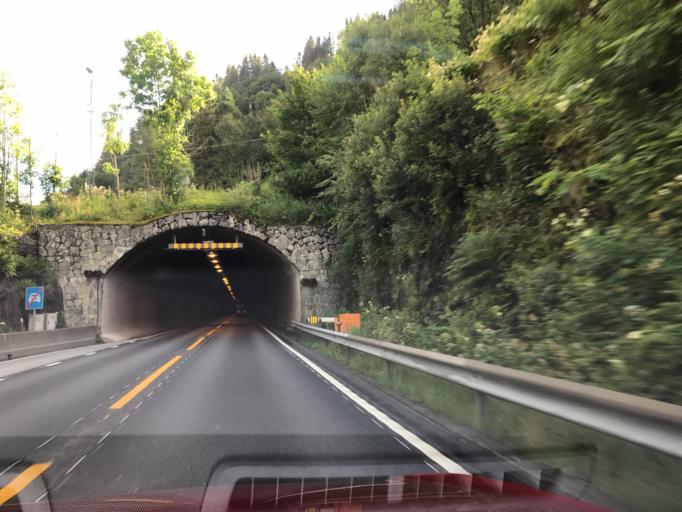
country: NO
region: Hordaland
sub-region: Bergen
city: Indre Arna
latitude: 60.4278
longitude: 5.5762
